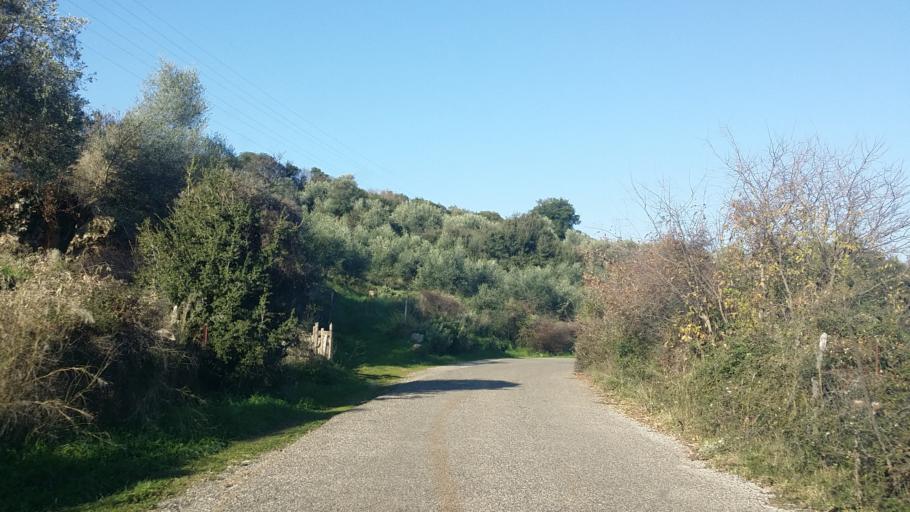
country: GR
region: West Greece
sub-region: Nomos Aitolias kai Akarnanias
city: Katouna
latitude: 38.7565
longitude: 21.1447
